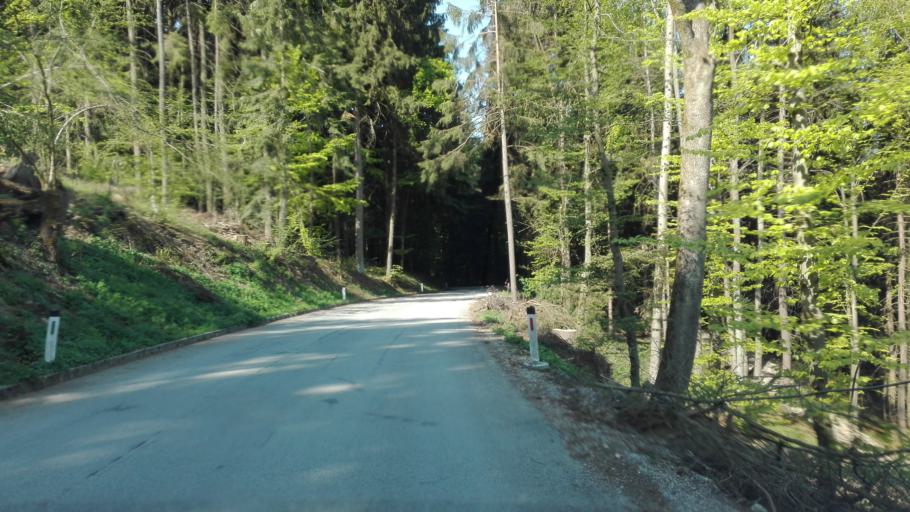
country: AT
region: Upper Austria
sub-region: Politischer Bezirk Rohrbach
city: Atzesberg
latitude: 48.4210
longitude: 13.9181
